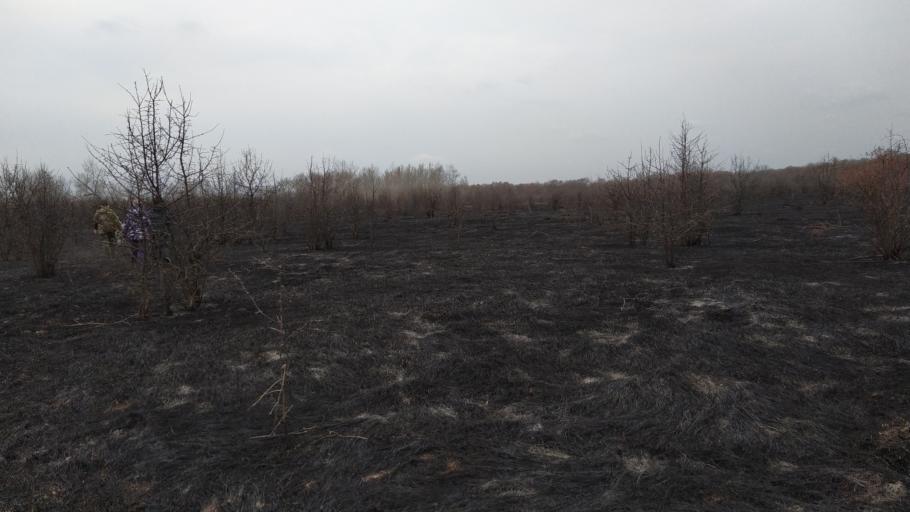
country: RU
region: Rostov
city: Semikarakorsk
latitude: 47.5426
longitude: 40.6840
